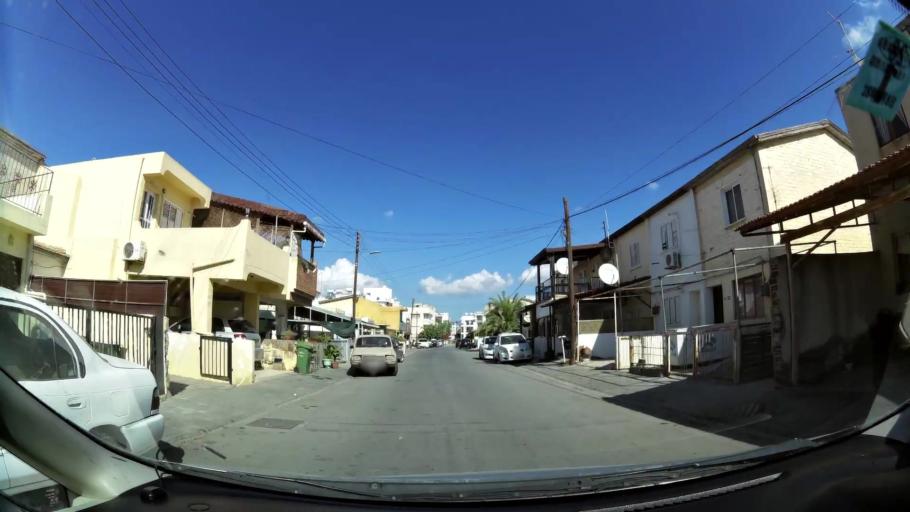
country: CY
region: Lefkosia
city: Nicosia
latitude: 35.2076
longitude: 33.3353
